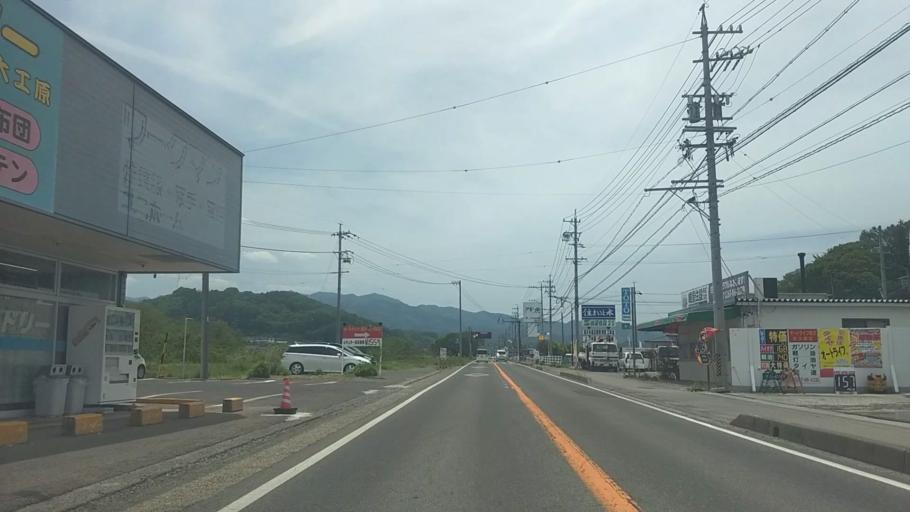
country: JP
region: Nagano
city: Saku
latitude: 36.1725
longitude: 138.4856
